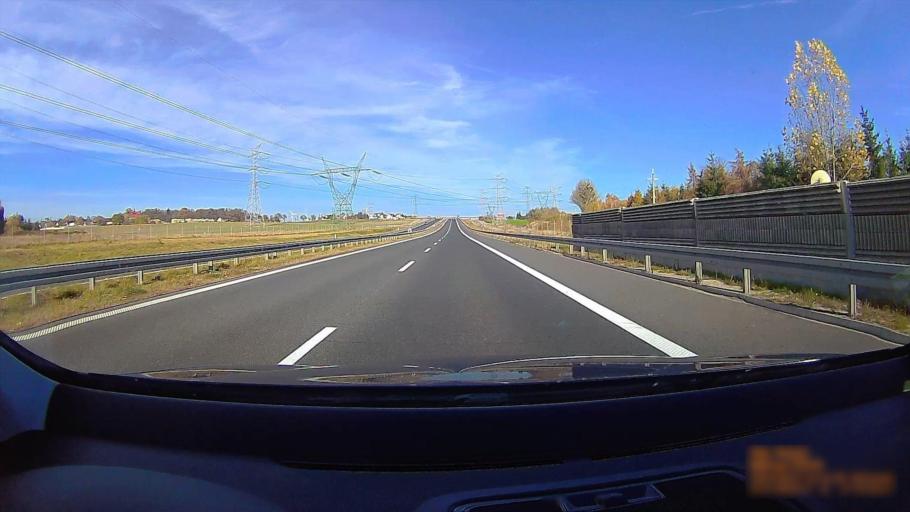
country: PL
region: Greater Poland Voivodeship
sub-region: Powiat ostrowski
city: Przygodzice
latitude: 51.6147
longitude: 17.8591
